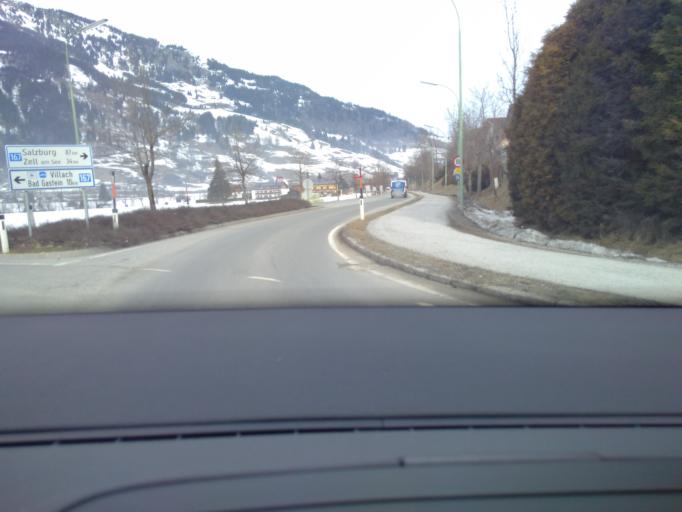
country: AT
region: Salzburg
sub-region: Politischer Bezirk Sankt Johann im Pongau
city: Bad Hofgastein
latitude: 47.1802
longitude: 13.1019
